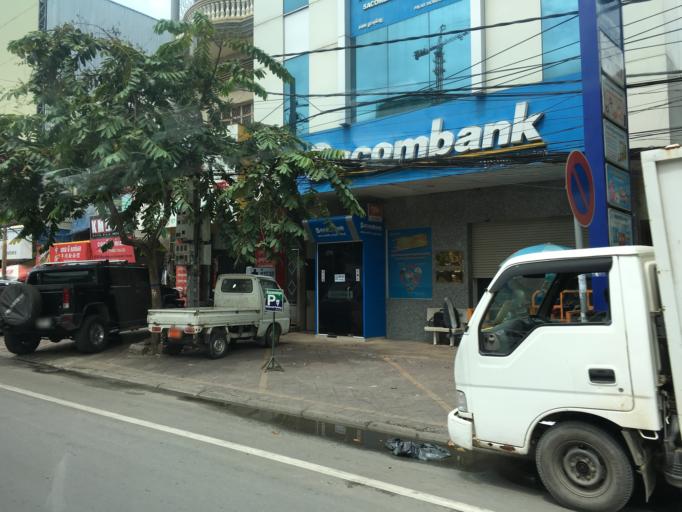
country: KH
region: Phnom Penh
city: Phnom Penh
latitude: 11.5532
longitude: 104.9209
